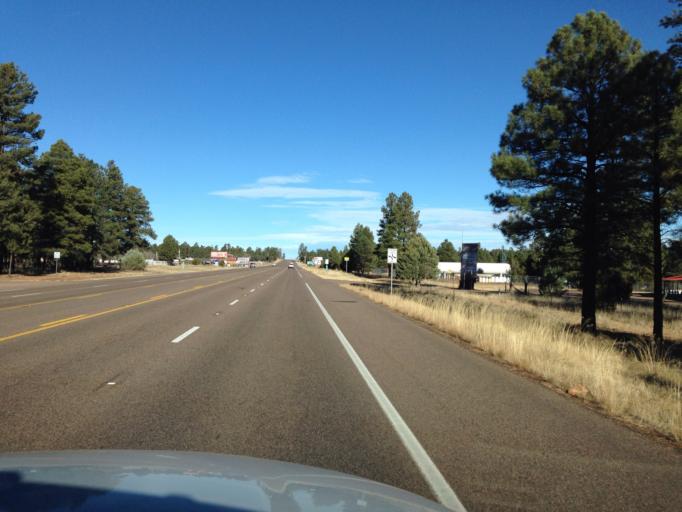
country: US
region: Arizona
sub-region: Navajo County
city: Heber-Overgaard
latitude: 34.4005
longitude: -110.5621
